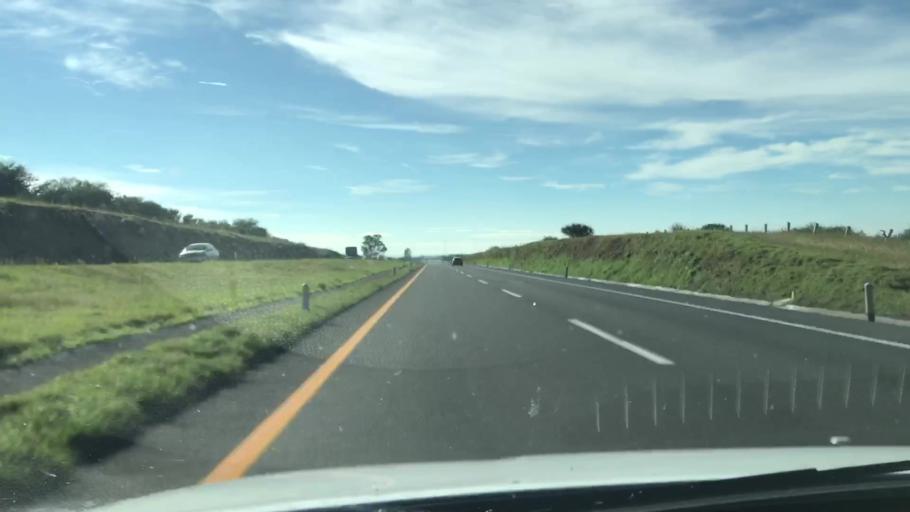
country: MX
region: Jalisco
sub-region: Union de San Antonio
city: San Jose del Caliche (El Caliche)
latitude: 21.2273
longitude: -101.9261
